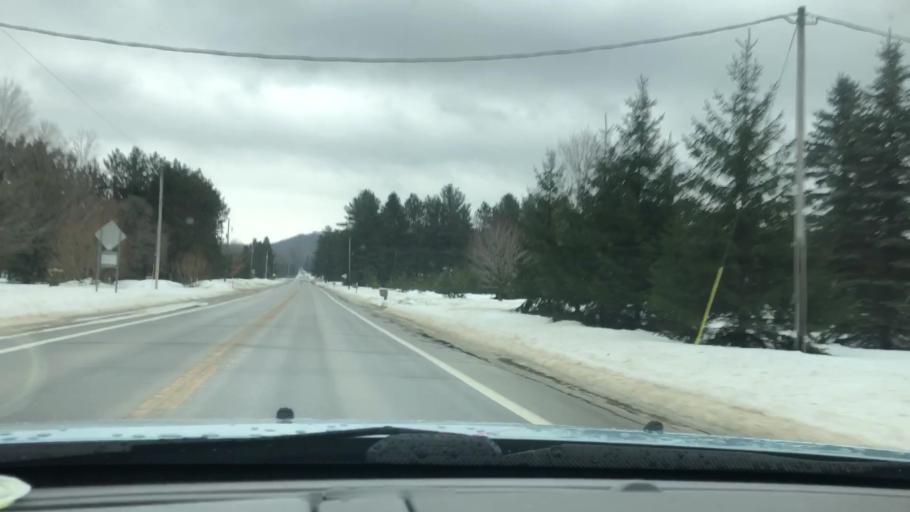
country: US
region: Michigan
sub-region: Charlevoix County
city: East Jordan
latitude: 45.1324
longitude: -85.0904
